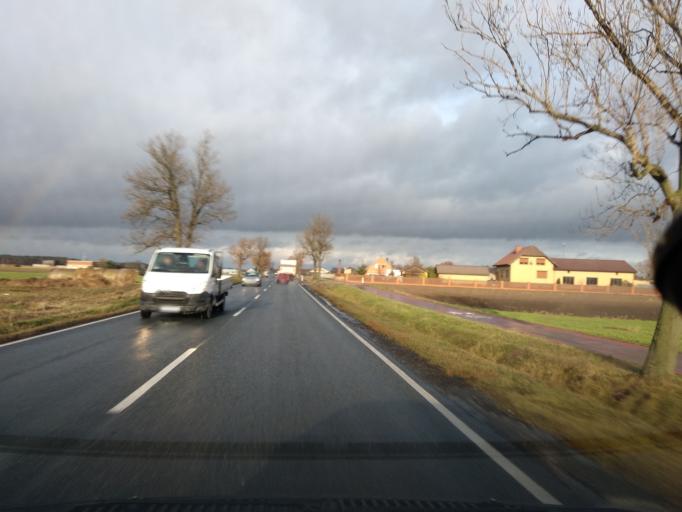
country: PL
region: Greater Poland Voivodeship
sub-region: Powiat koninski
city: Rychwal
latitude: 52.1110
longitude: 18.1676
